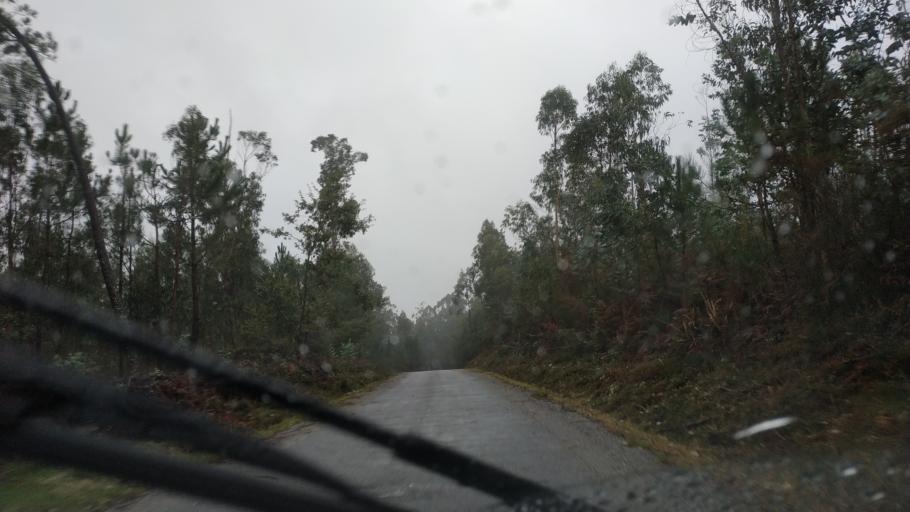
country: ES
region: Galicia
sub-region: Provincia da Coruna
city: Negreira
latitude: 42.9099
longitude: -8.7676
